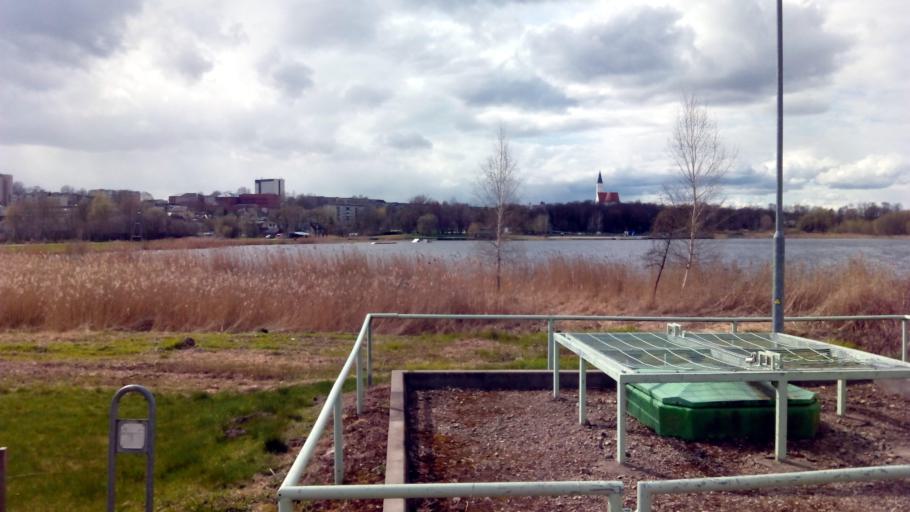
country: LT
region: Siauliu apskritis
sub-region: Siauliai
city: Siauliai
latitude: 55.9293
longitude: 23.3355
